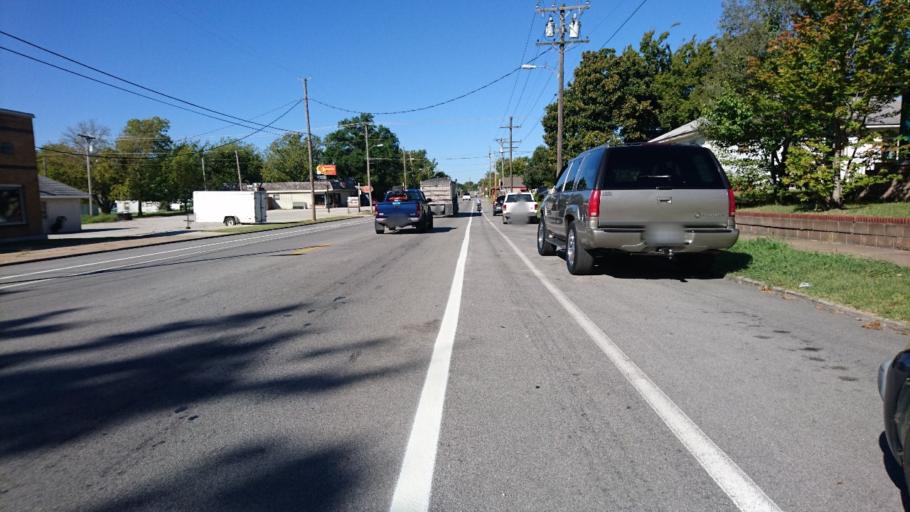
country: US
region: Missouri
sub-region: Jasper County
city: Joplin
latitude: 37.0919
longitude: -94.4972
